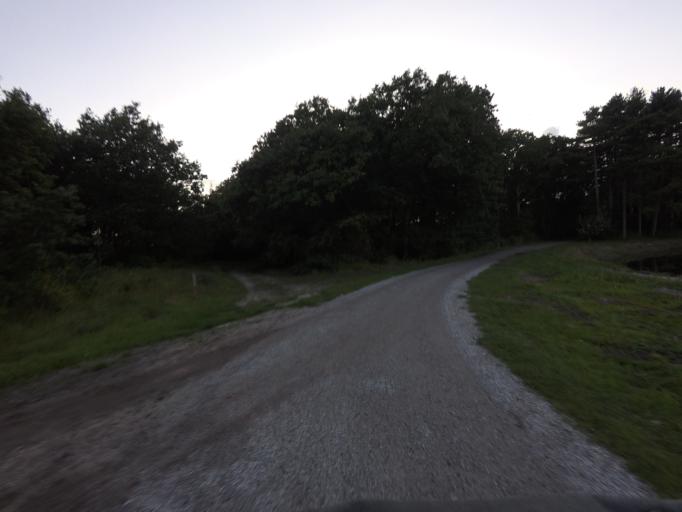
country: NL
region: Friesland
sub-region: Gemeente Terschelling
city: West-Terschelling
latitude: 53.3658
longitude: 5.2076
